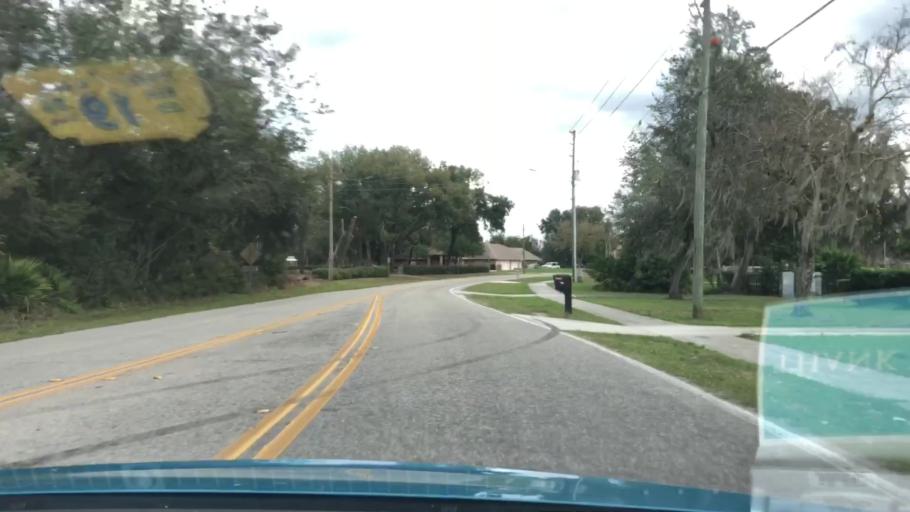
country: US
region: Florida
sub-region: Volusia County
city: Deltona
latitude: 28.8837
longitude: -81.2226
